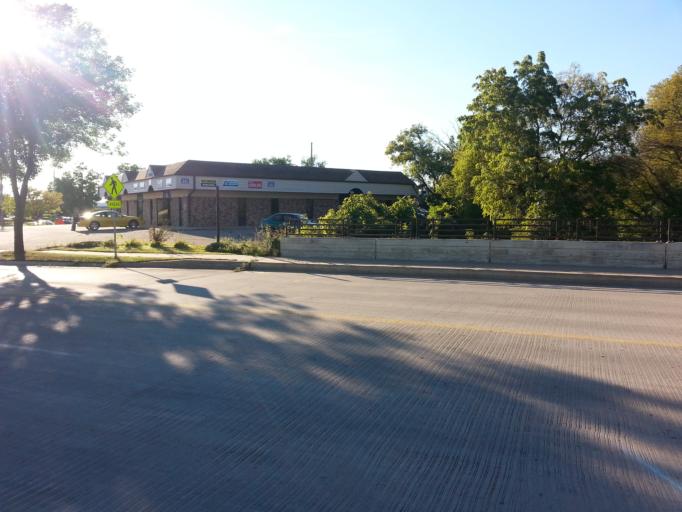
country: US
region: Minnesota
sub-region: Olmsted County
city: Rochester
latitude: 44.0280
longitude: -92.4844
